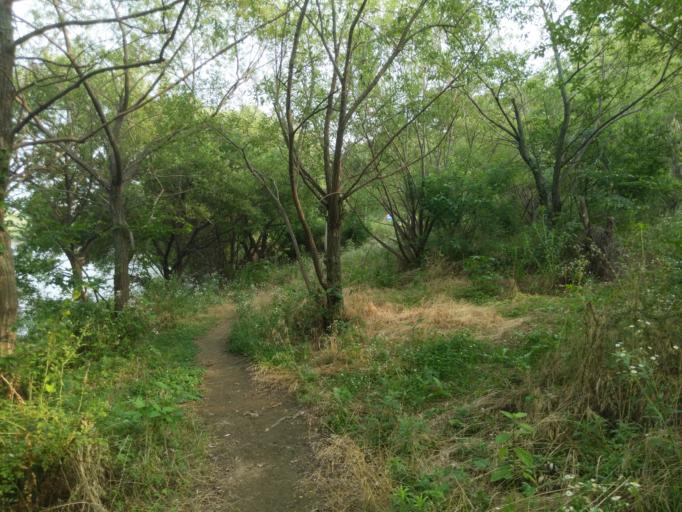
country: KR
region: Gyeonggi-do
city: Kwangmyong
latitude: 37.5365
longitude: 126.9064
